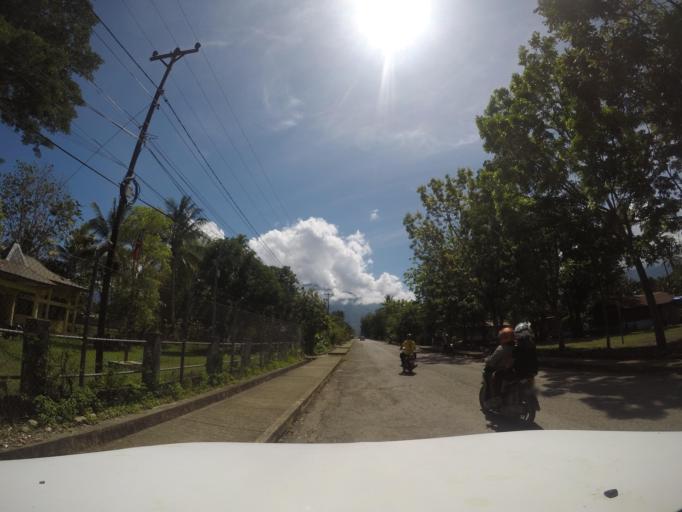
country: TL
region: Bobonaro
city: Maliana
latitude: -8.9901
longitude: 125.2046
